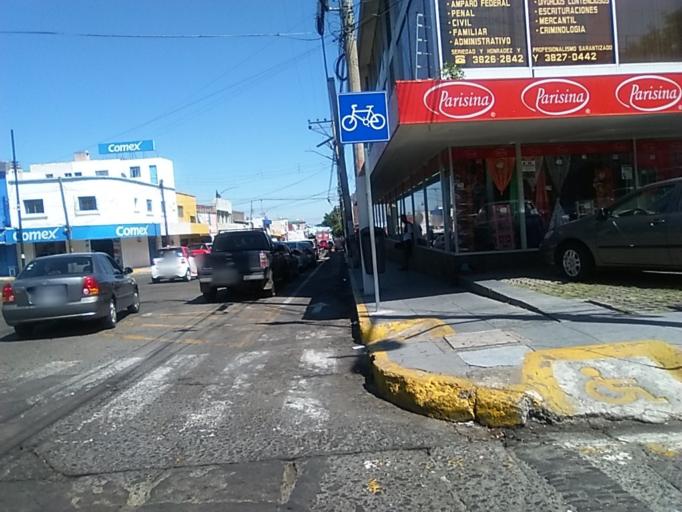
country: MX
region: Jalisco
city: Guadalajara
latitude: 20.6788
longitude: -103.3686
